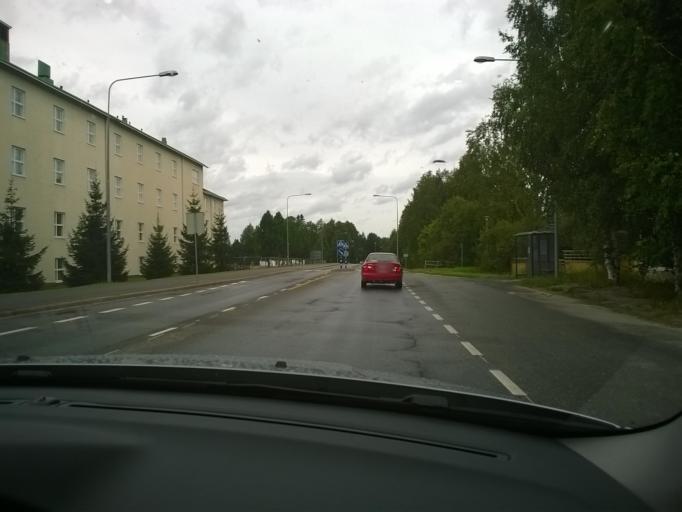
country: FI
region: Kainuu
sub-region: Kehys-Kainuu
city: Kuhmo
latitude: 64.1239
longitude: 29.5094
